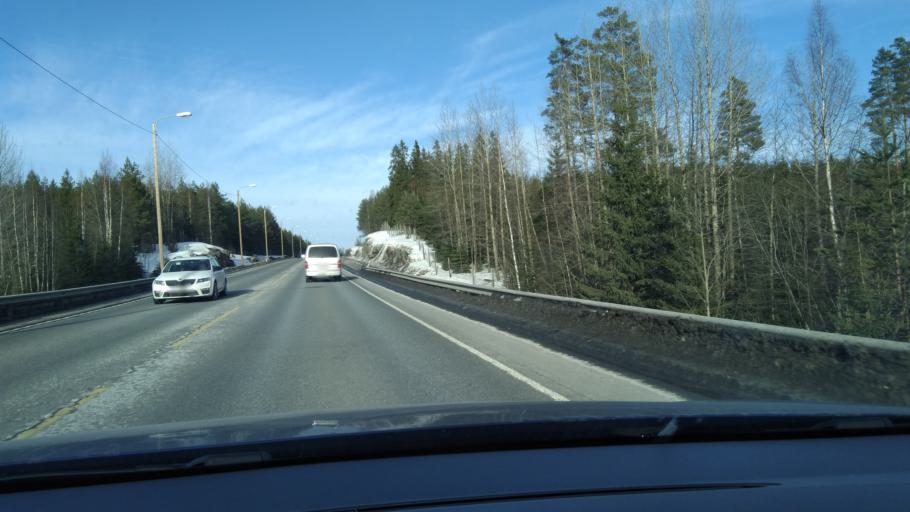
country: FI
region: Pirkanmaa
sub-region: Tampere
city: Orivesi
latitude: 61.6637
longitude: 24.2660
